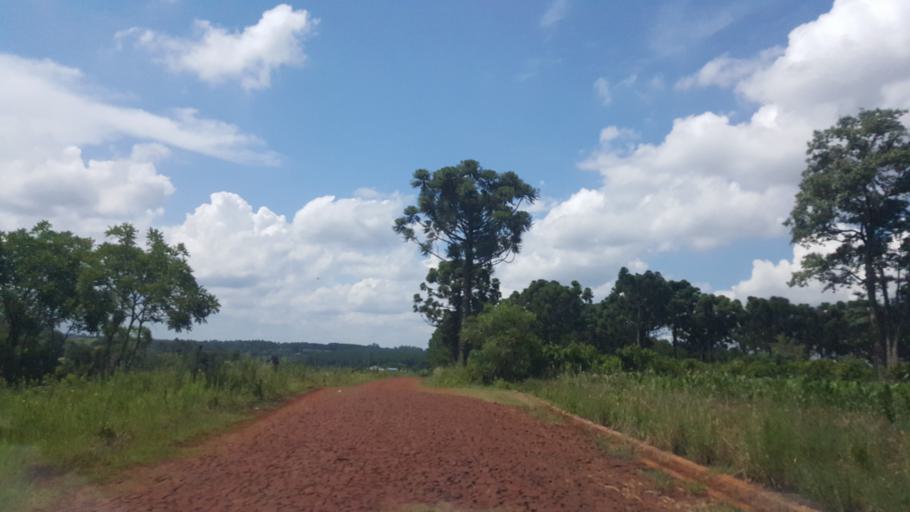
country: AR
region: Misiones
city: Capiovi
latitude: -26.9285
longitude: -55.0418
